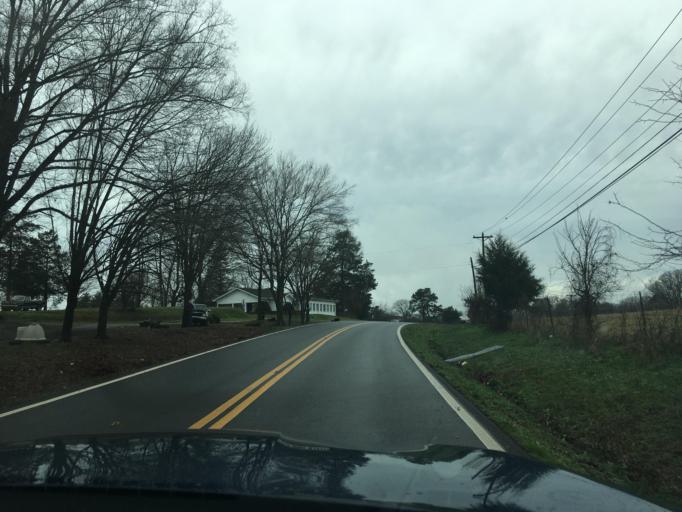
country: US
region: Tennessee
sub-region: McMinn County
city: Englewood
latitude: 35.4215
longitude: -84.4792
